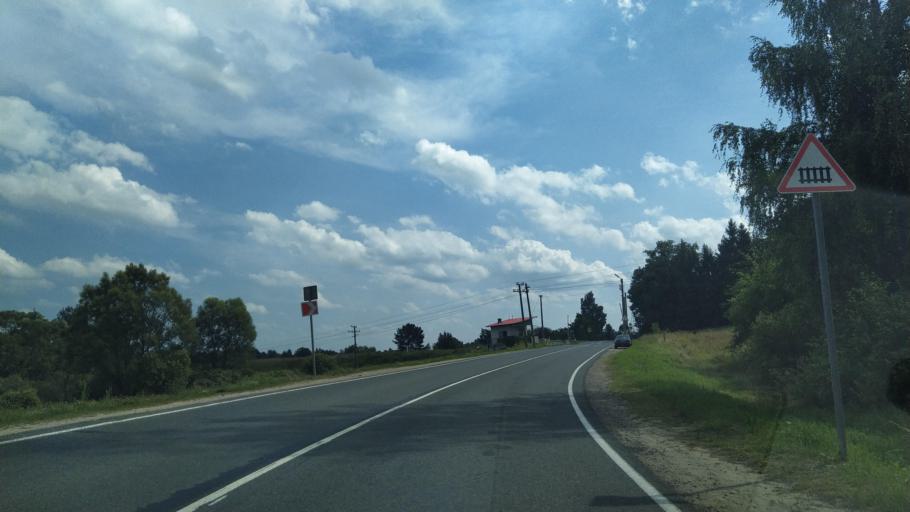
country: RU
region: Pskov
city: Pskov
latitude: 57.7596
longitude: 28.7703
